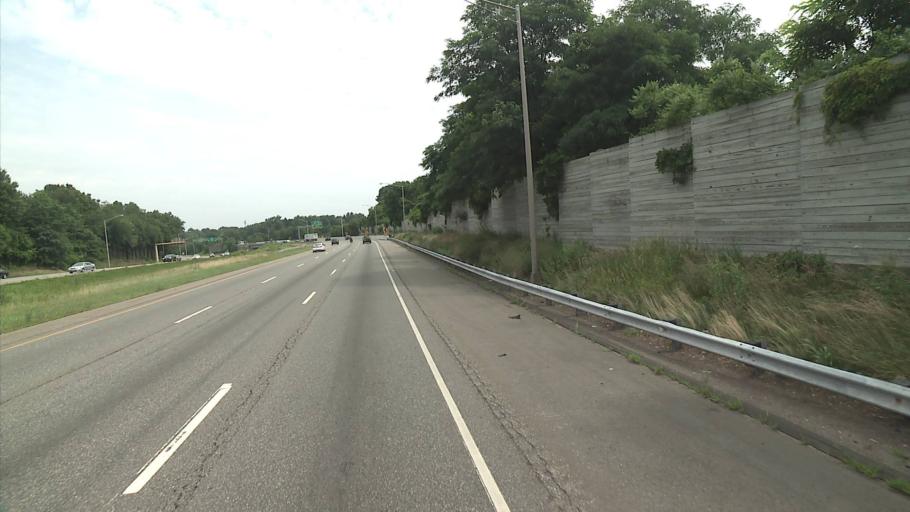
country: US
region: Connecticut
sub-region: Hartford County
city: West Hartford
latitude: 41.7400
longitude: -72.7367
